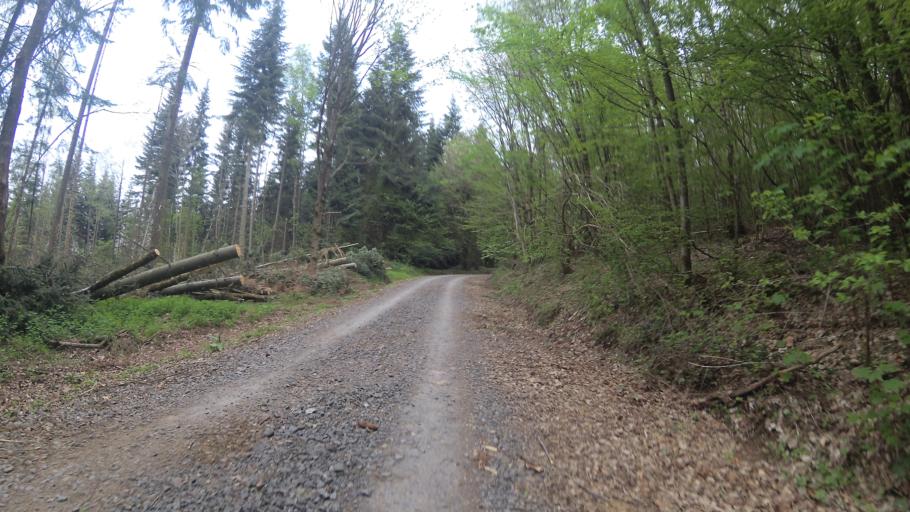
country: DE
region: Saarland
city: Mainzweiler
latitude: 49.4227
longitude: 7.1309
